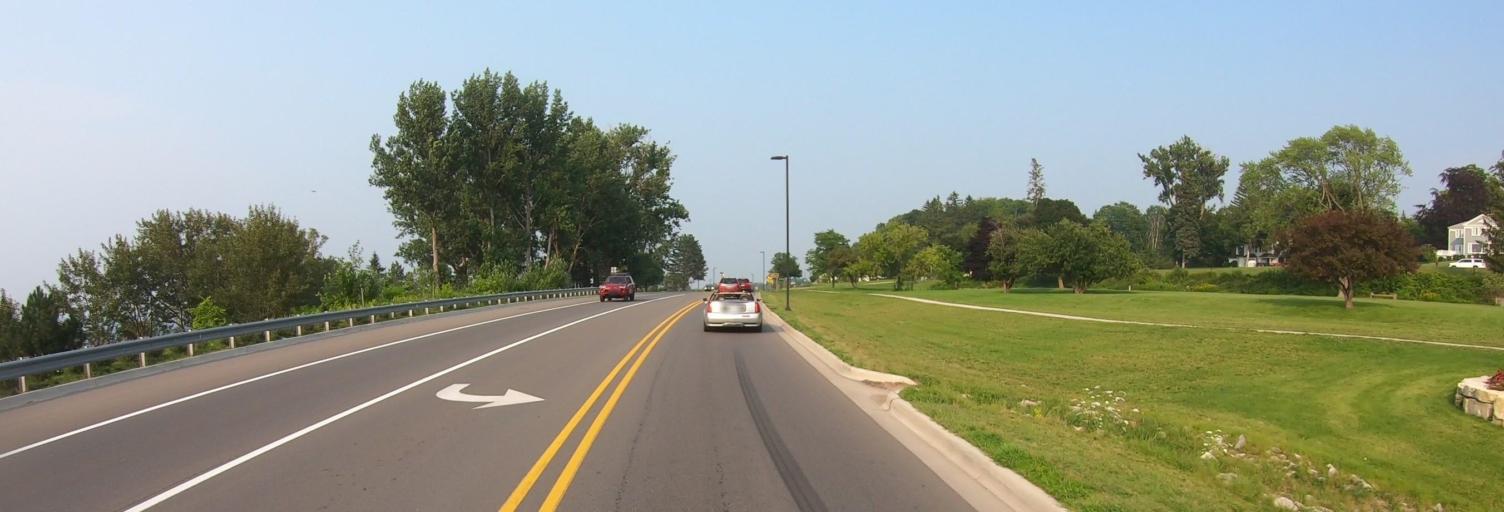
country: US
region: Michigan
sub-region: Emmet County
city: Petoskey
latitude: 45.3782
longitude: -84.9552
